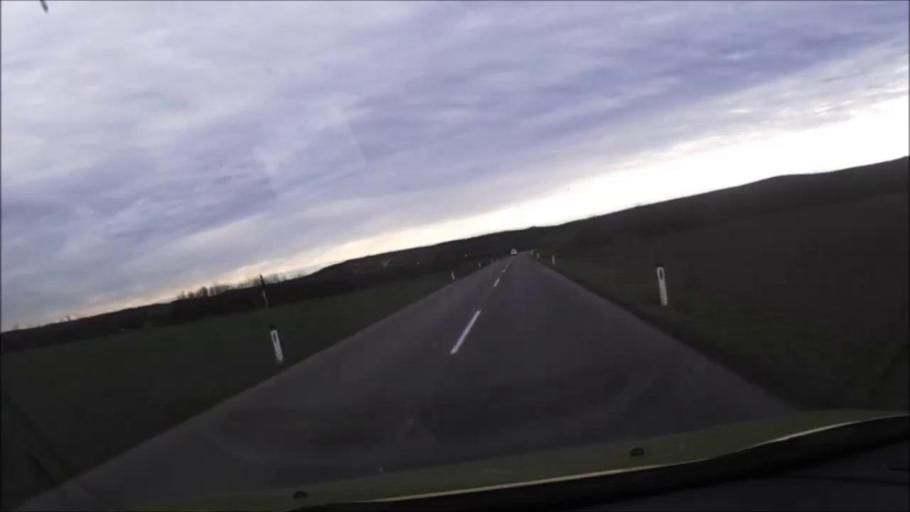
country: AT
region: Burgenland
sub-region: Eisenstadt-Umgebung
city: Loretto
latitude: 47.9263
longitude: 16.4997
